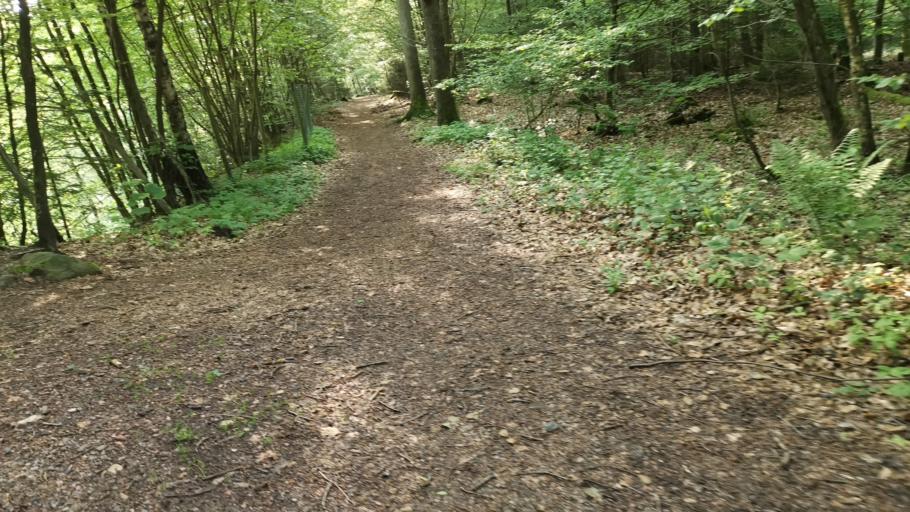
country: DE
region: Saarland
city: Kirkel
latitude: 49.2734
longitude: 7.1756
